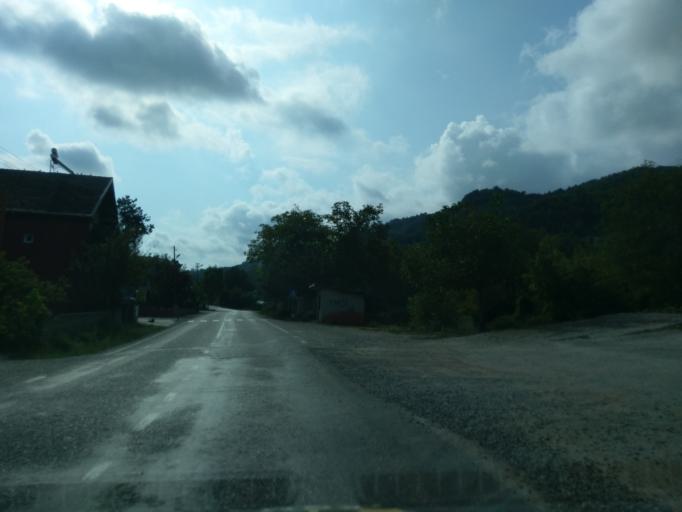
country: TR
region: Sinop
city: Helaldi
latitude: 41.9049
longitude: 34.4449
